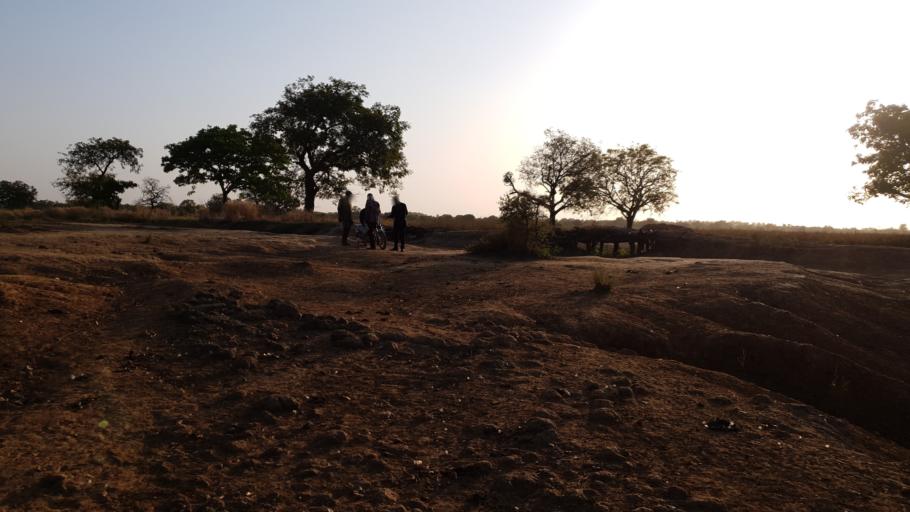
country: ML
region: Sikasso
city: Kadiolo
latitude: 10.6627
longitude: -5.8037
